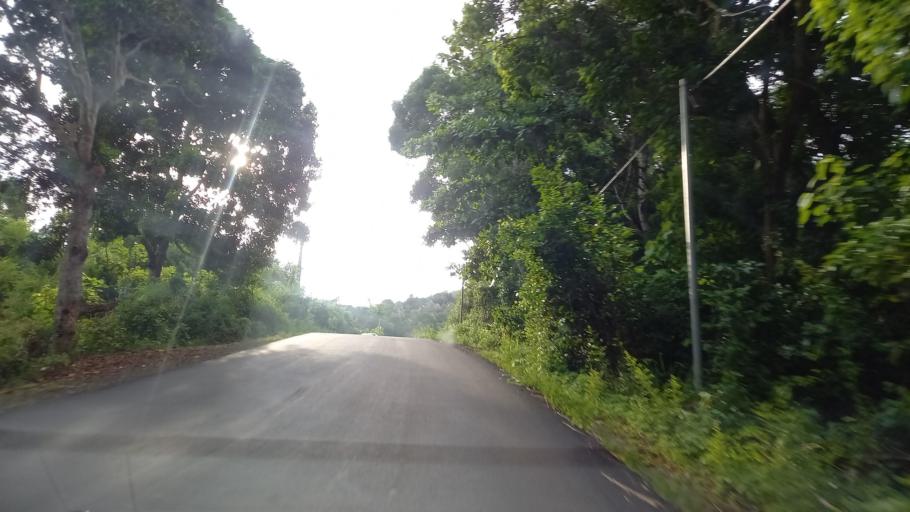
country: YT
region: Acoua
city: Acoua
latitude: -12.7470
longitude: 45.0587
